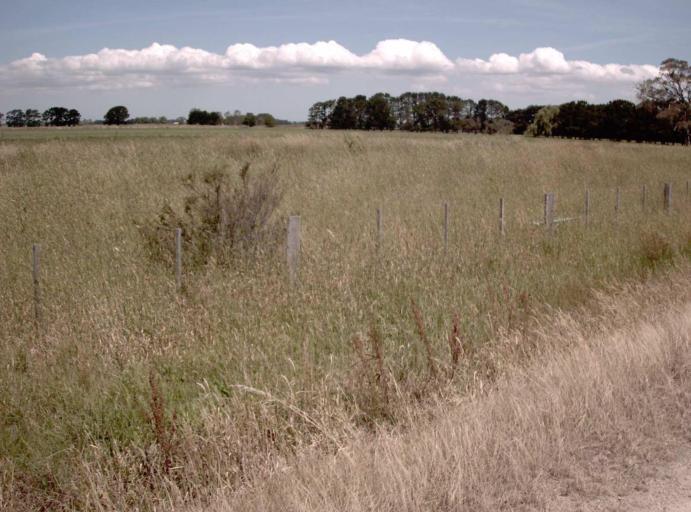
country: AU
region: Victoria
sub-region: Wellington
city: Heyfield
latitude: -38.0324
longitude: 146.8789
